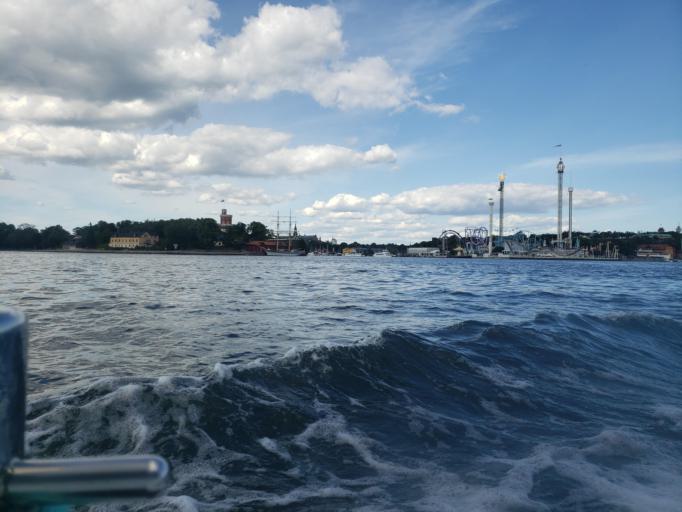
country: SE
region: Stockholm
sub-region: Stockholms Kommun
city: OEstermalm
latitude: 59.3188
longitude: 18.0897
